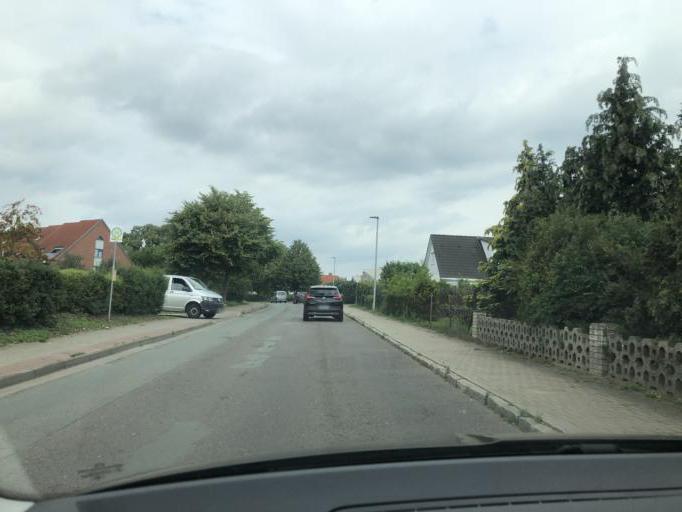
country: DE
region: Mecklenburg-Vorpommern
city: Klein Rogahn
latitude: 53.5688
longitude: 11.3567
